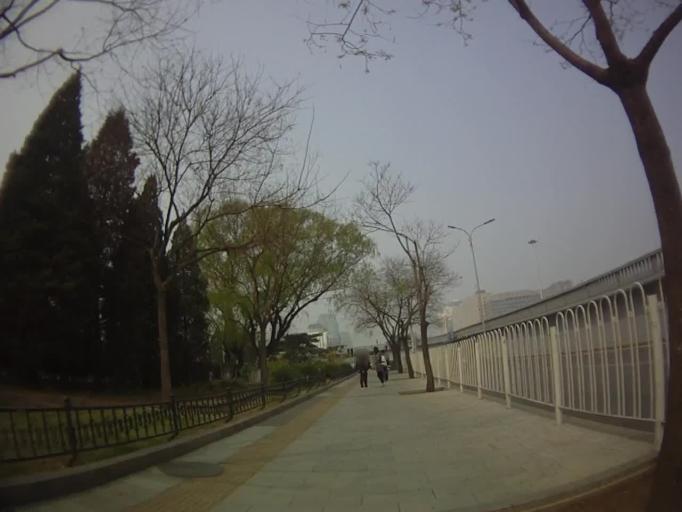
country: CN
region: Beijing
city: Chaowai
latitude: 39.9068
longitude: 116.4318
